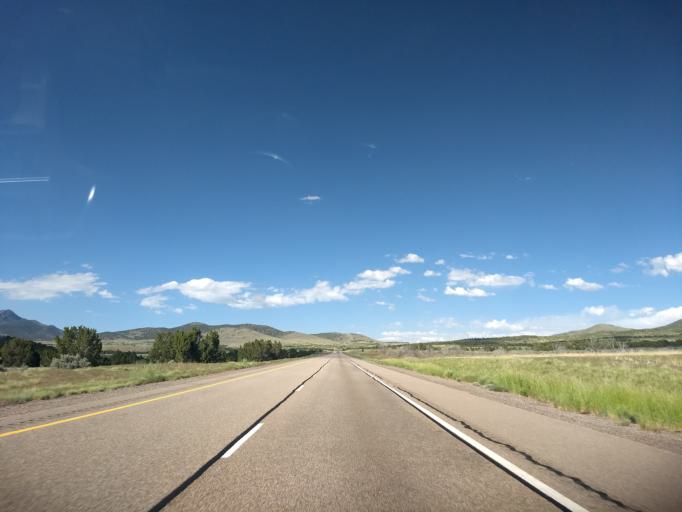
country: US
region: Utah
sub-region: Millard County
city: Fillmore
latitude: 39.1732
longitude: -112.2106
